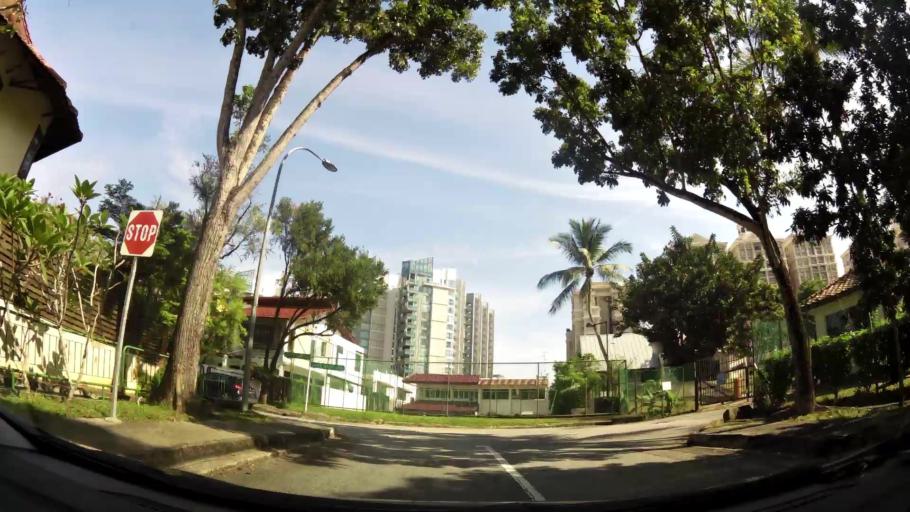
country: SG
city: Singapore
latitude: 1.3635
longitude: 103.8298
